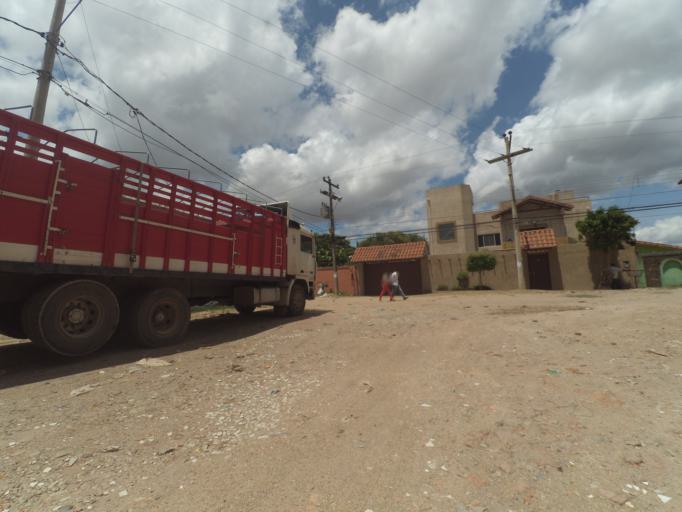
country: BO
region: Santa Cruz
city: Santa Cruz de la Sierra
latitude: -17.8137
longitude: -63.2139
